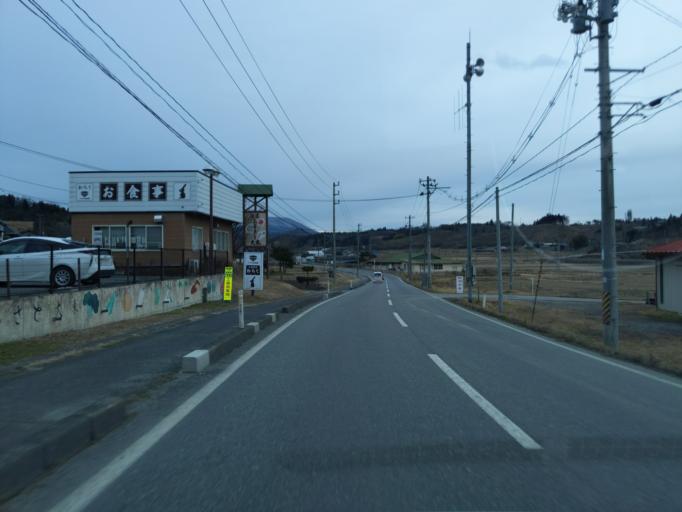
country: JP
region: Iwate
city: Ichinoseki
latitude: 39.0222
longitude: 141.3275
